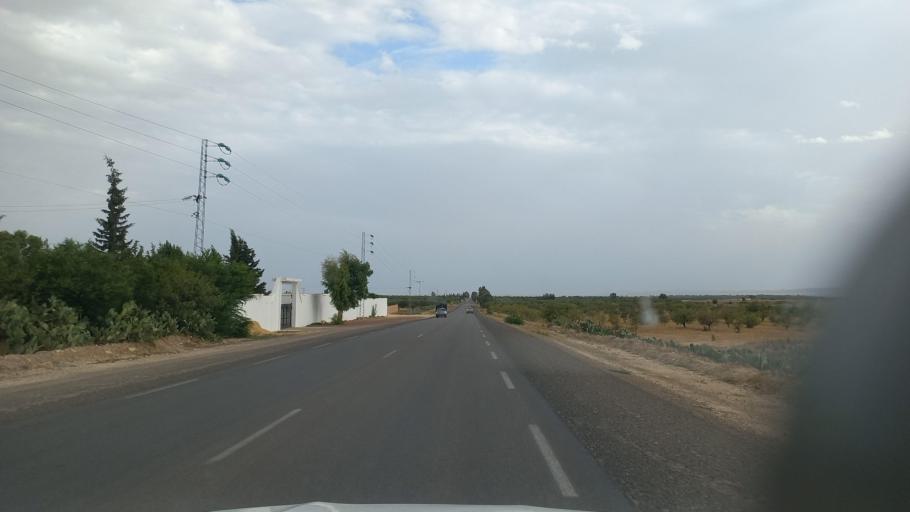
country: TN
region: Al Qasrayn
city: Sbiba
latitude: 35.3130
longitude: 9.0846
